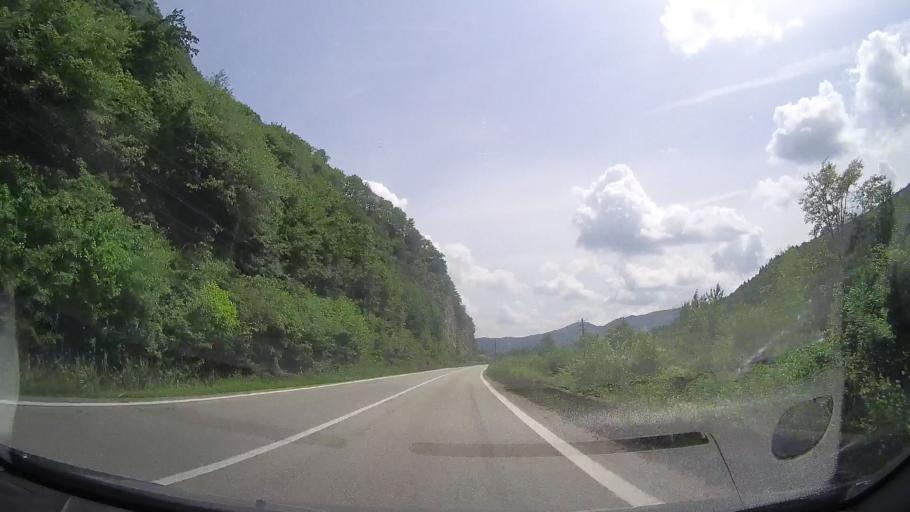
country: RO
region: Valcea
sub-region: Oras Calimanesti
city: Jiblea Veche
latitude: 45.2535
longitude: 24.3388
